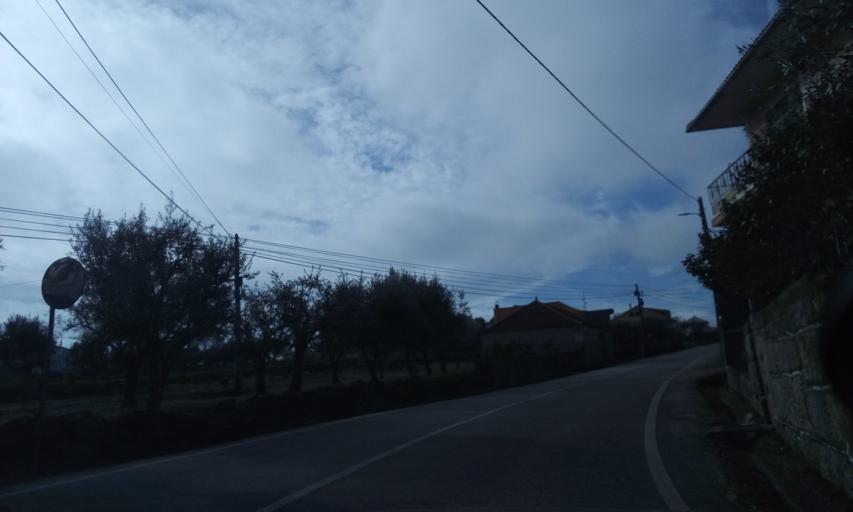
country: PT
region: Guarda
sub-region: Aguiar da Beira
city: Aguiar da Beira
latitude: 40.7629
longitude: -7.5404
